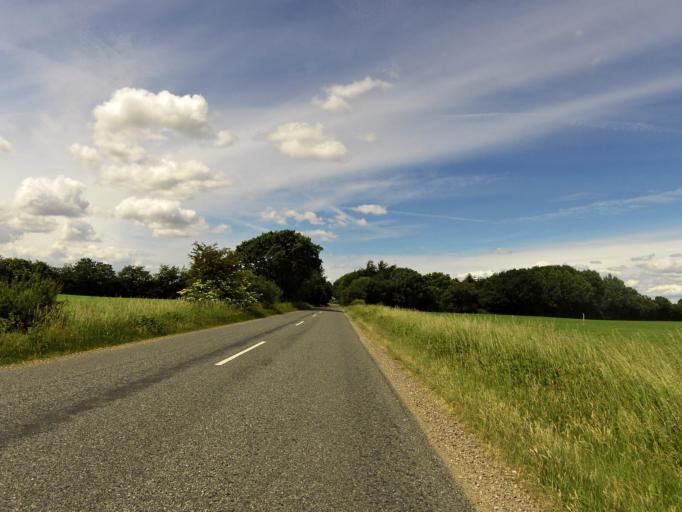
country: DK
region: South Denmark
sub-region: Esbjerg Kommune
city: Ribe
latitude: 55.2766
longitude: 8.7987
